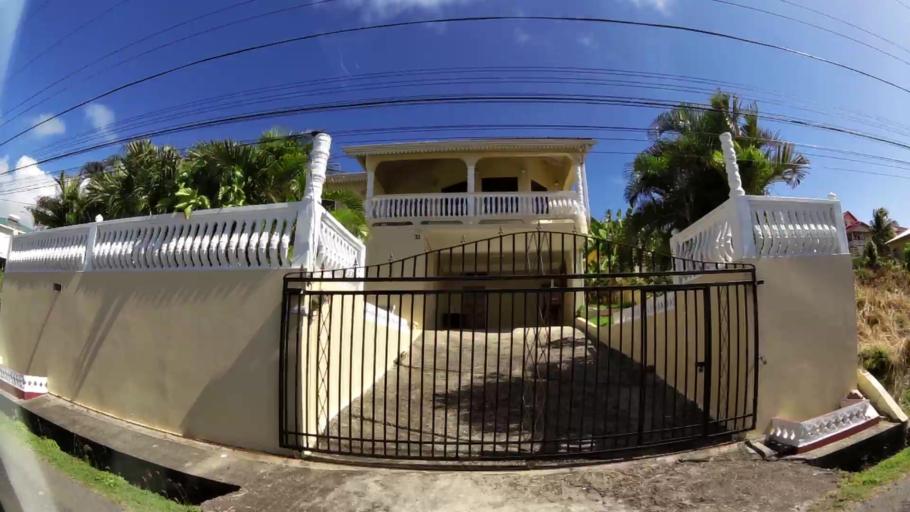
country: LC
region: Laborie Quarter
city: Laborie
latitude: 13.7397
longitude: -60.9685
